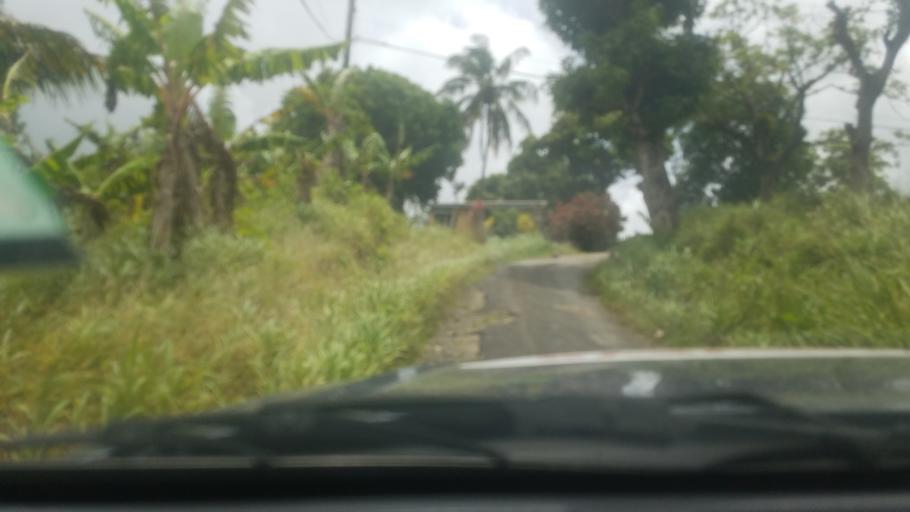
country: LC
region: Laborie Quarter
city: Laborie
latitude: 13.7805
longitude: -60.9861
